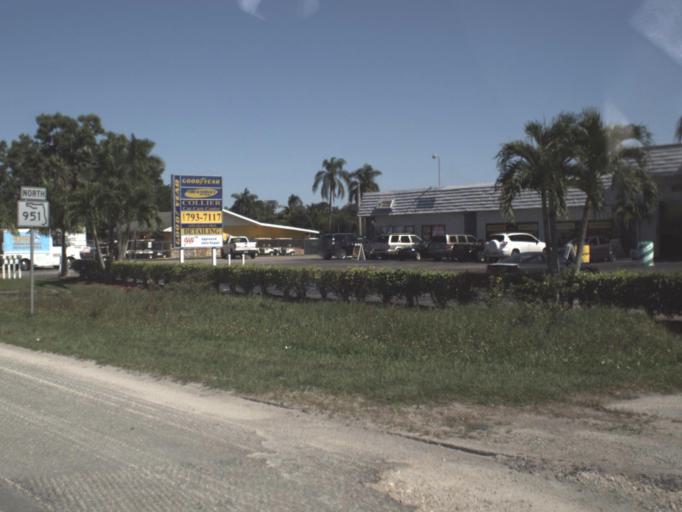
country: US
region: Florida
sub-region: Collier County
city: Lely Resort
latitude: 26.0484
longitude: -81.6998
